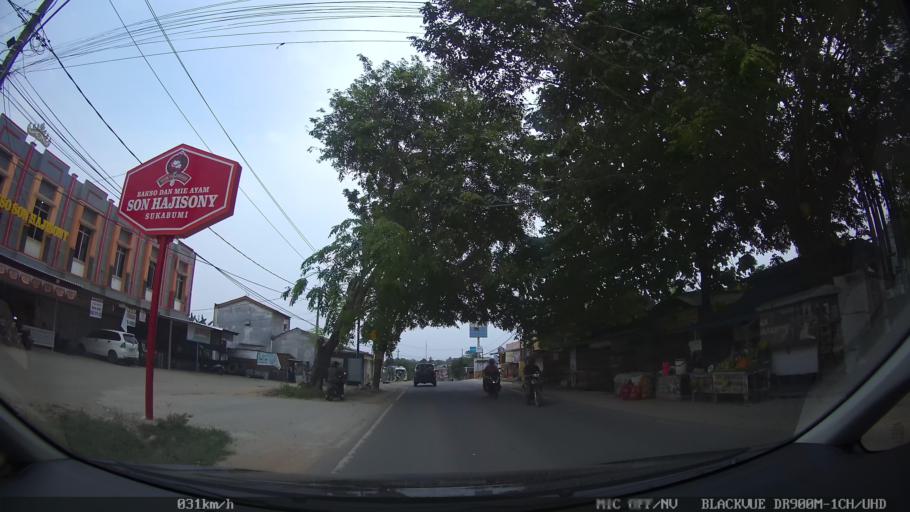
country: ID
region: Lampung
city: Kedaton
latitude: -5.4003
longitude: 105.3101
